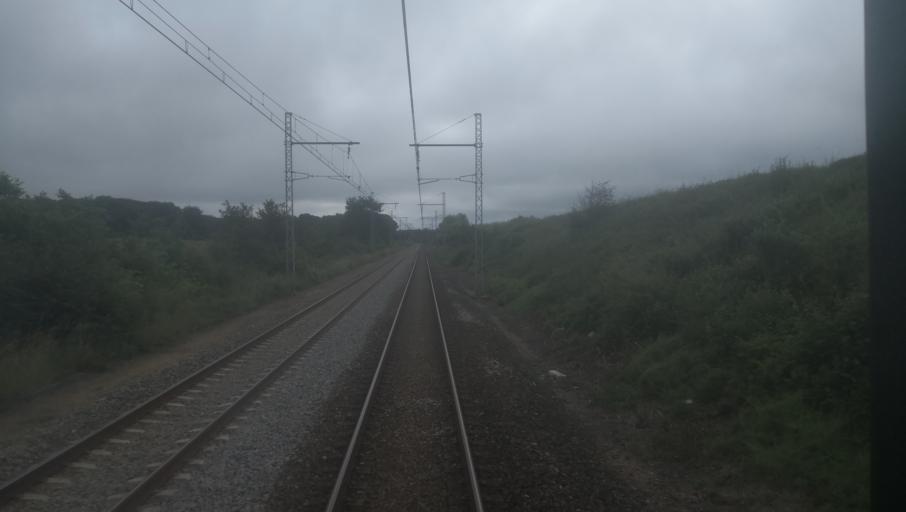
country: FR
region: Centre
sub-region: Departement de l'Indre
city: Saint-Maur
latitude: 46.7691
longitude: 1.6185
